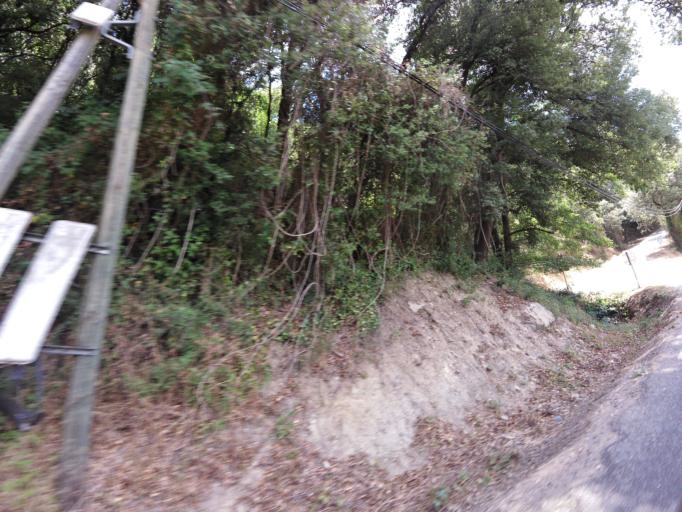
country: FR
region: Languedoc-Roussillon
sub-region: Departement du Gard
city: Sumene
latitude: 43.9811
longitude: 3.6924
